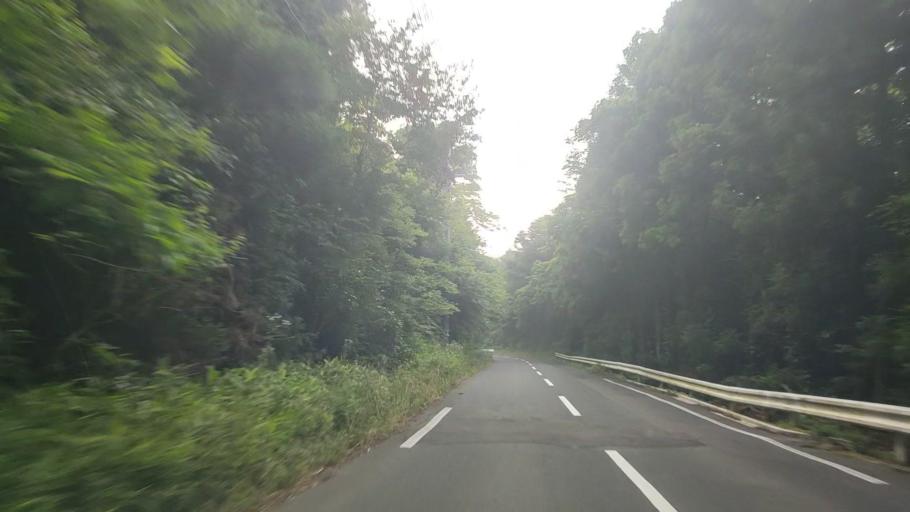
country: JP
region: Tottori
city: Kurayoshi
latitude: 35.4020
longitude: 133.7756
